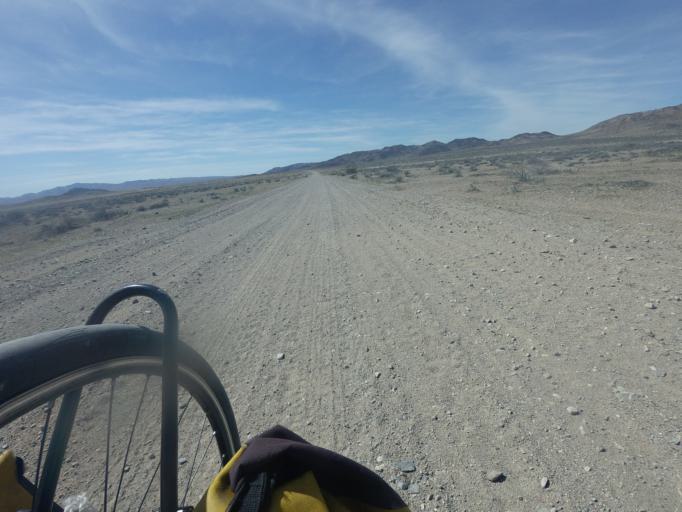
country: US
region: California
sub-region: San Bernardino County
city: Searles Valley
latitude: 35.5952
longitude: -117.4062
